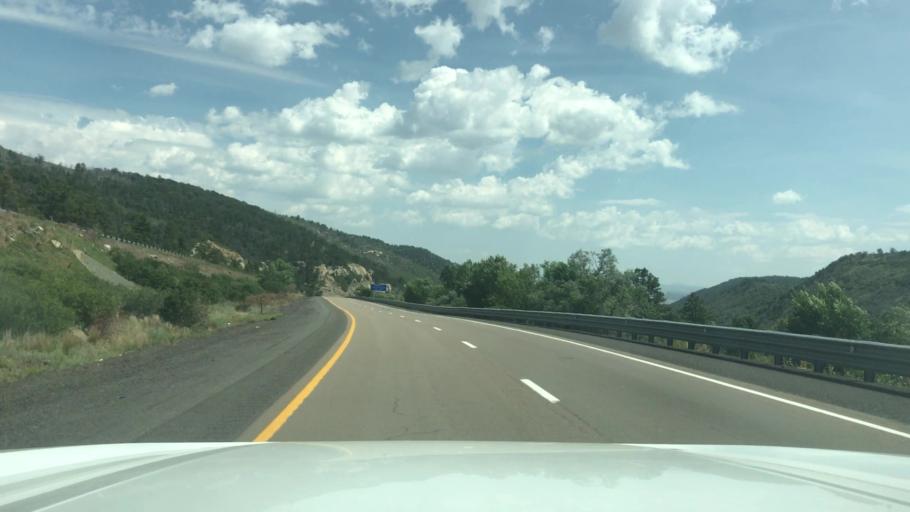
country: US
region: New Mexico
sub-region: Colfax County
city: Raton
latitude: 36.9349
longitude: -104.4642
